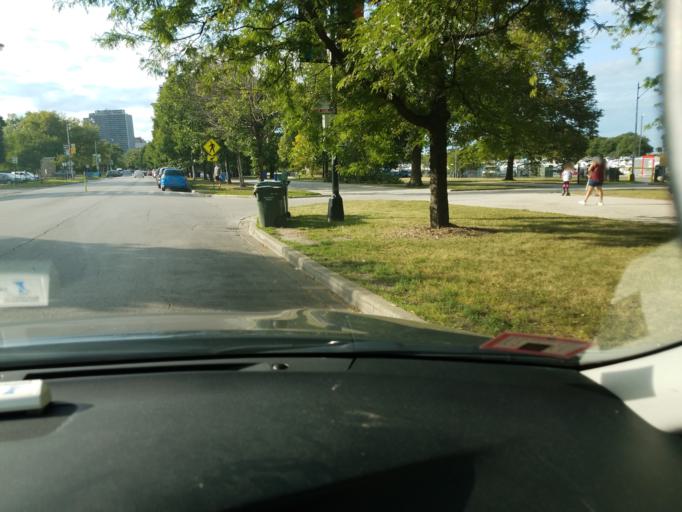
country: US
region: Illinois
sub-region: Cook County
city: Chicago
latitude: 41.9265
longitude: -87.6340
